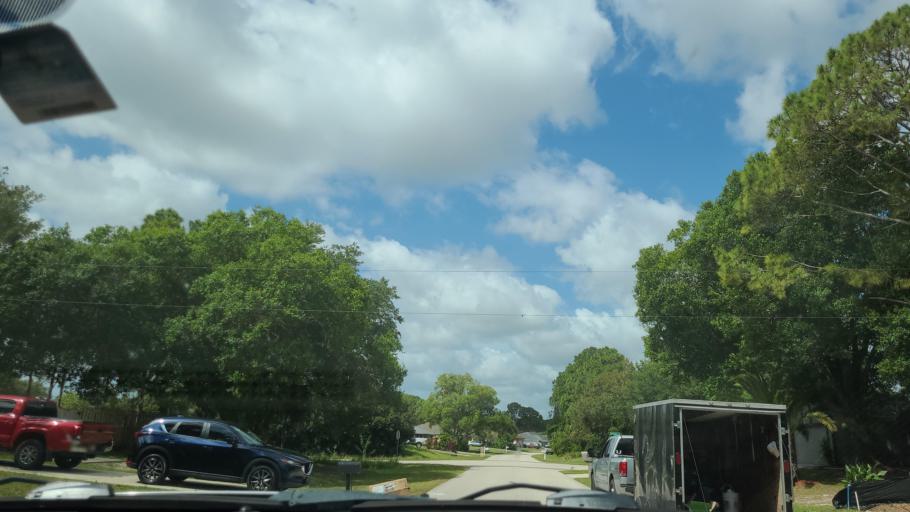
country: US
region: Florida
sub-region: Brevard County
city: Grant-Valkaria
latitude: 27.9667
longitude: -80.6636
